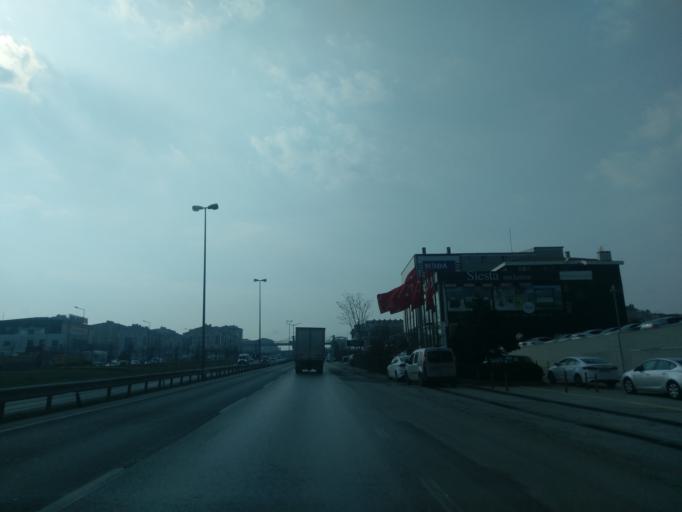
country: TR
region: Istanbul
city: Chekmejeh
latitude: 41.0139
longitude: 28.5430
